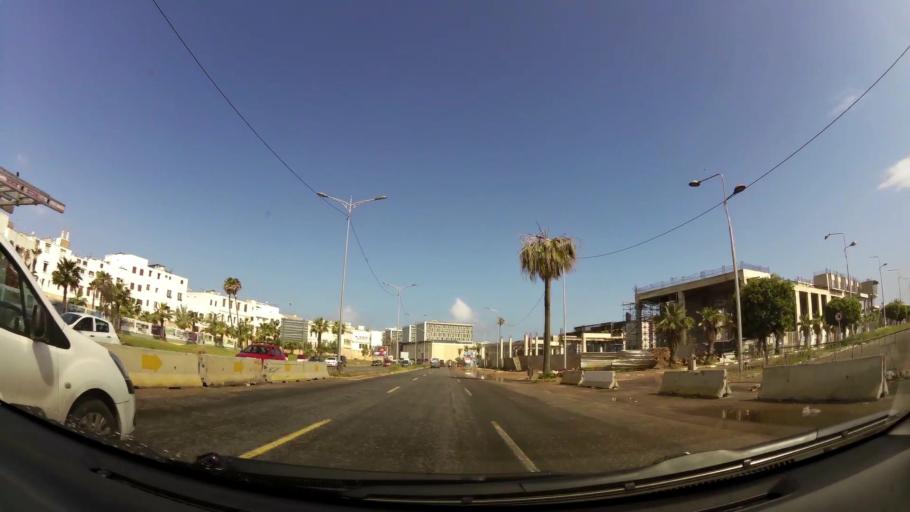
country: MA
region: Grand Casablanca
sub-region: Casablanca
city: Casablanca
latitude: 33.6033
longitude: -7.6188
